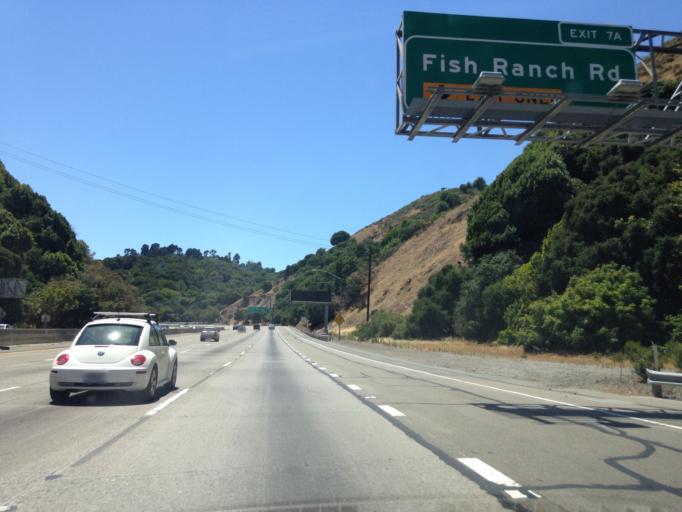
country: US
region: California
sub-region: Contra Costa County
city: Orinda
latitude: 37.8670
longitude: -122.2043
